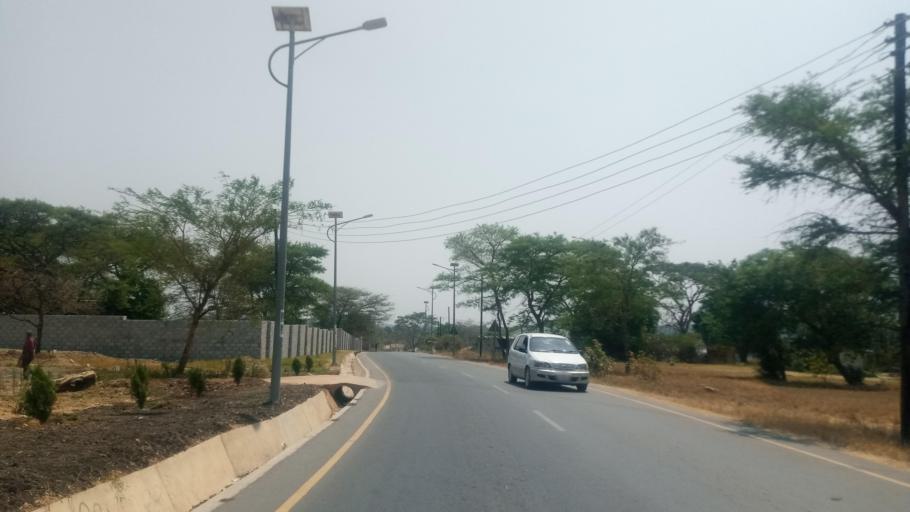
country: ZM
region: Lusaka
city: Lusaka
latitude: -15.4531
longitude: 28.4407
